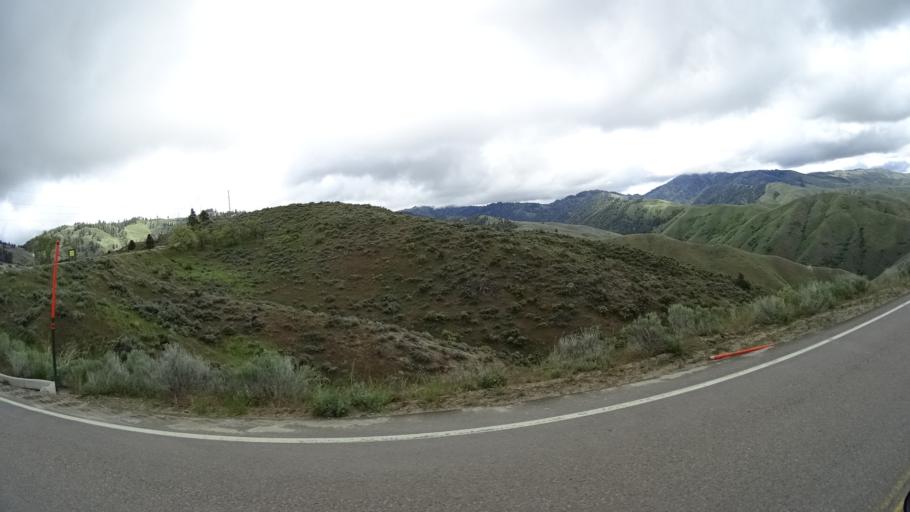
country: US
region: Idaho
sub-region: Ada County
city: Boise
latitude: 43.7220
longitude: -116.1610
